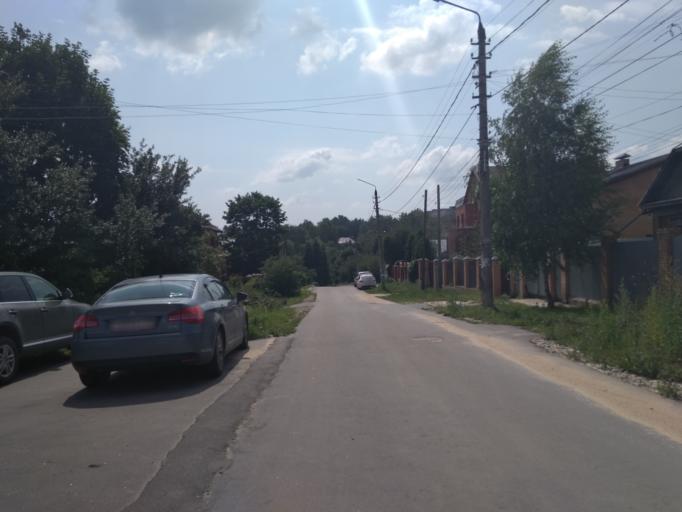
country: RU
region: Tula
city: Tula
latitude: 54.1637
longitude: 37.6111
